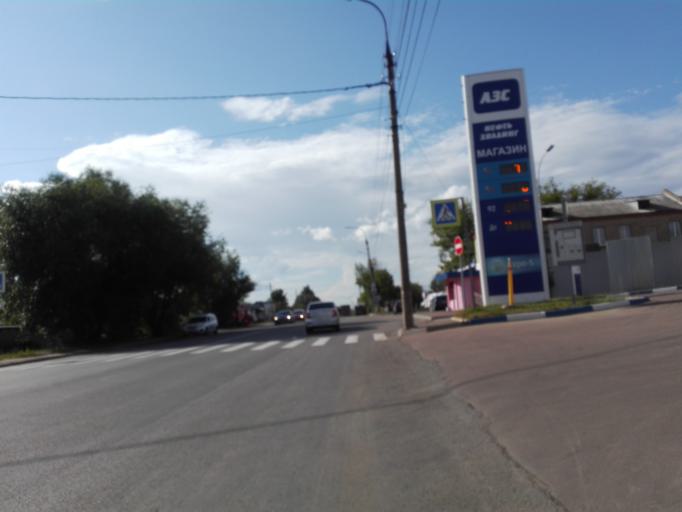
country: RU
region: Orjol
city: Orel
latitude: 52.9928
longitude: 36.1154
